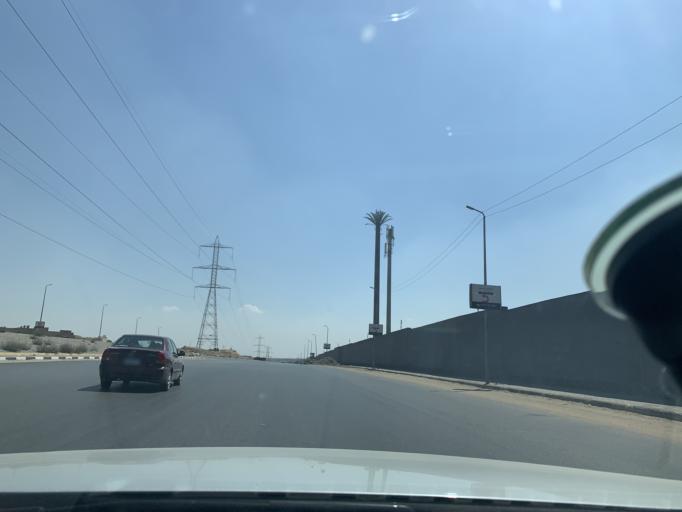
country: EG
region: Muhafazat al Qahirah
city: Cairo
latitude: 30.0339
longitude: 31.3527
